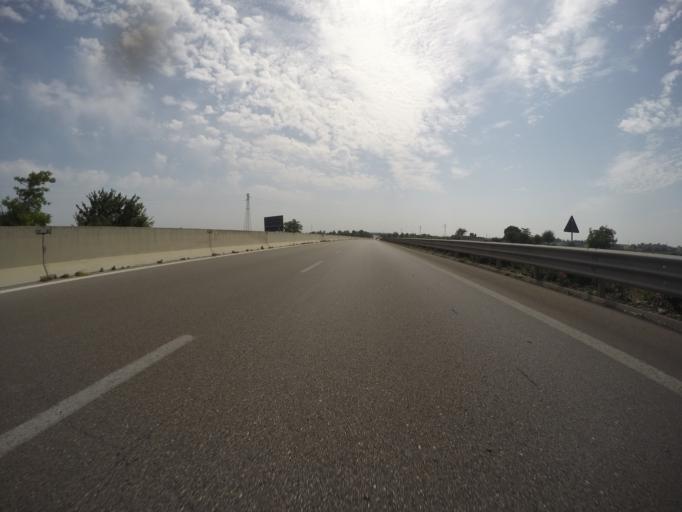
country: IT
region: Apulia
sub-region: Provincia di Brindisi
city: Francavilla Fontana
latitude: 40.5465
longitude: 17.5800
